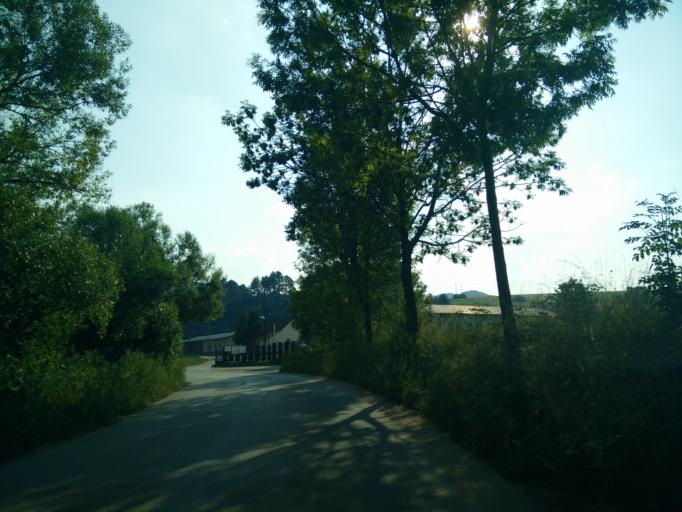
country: SK
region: Zilinsky
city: Rajec
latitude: 49.0678
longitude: 18.6271
